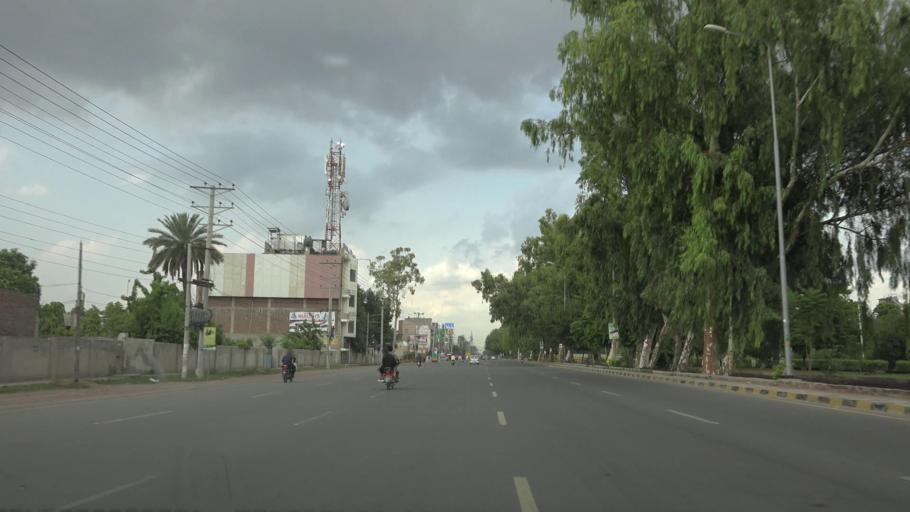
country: PK
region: Punjab
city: Faisalabad
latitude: 31.4282
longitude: 73.1173
